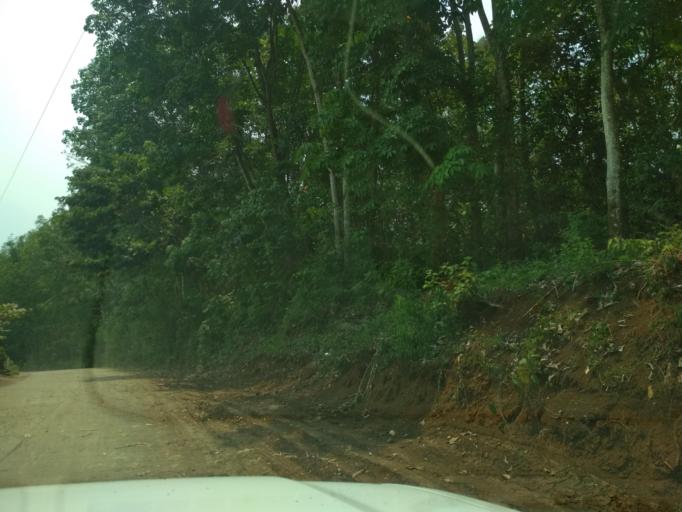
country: MX
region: Veracruz
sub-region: Tezonapa
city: Laguna Chica (Pueblo Nuevo)
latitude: 18.5429
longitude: -96.7848
